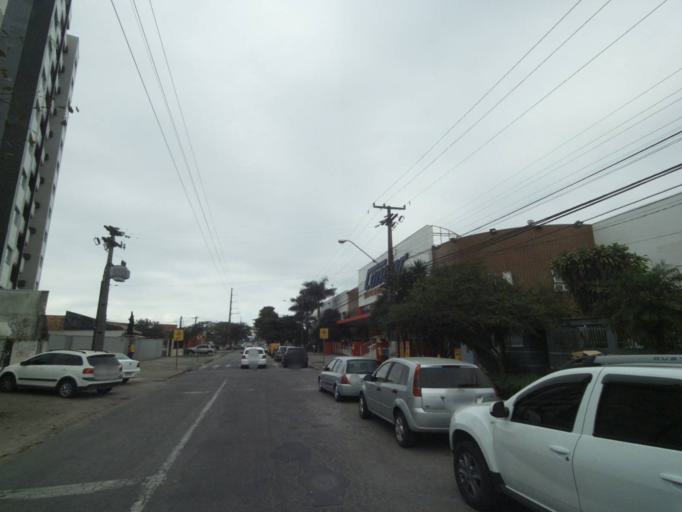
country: BR
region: Parana
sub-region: Paranagua
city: Paranagua
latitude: -25.5192
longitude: -48.5197
